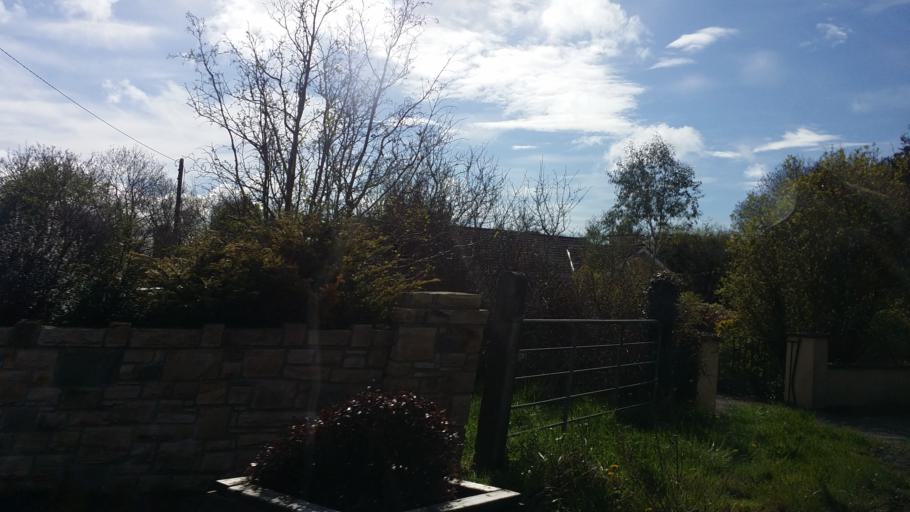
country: IE
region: Ulster
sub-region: County Donegal
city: Ballyshannon
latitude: 54.4902
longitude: -8.1482
